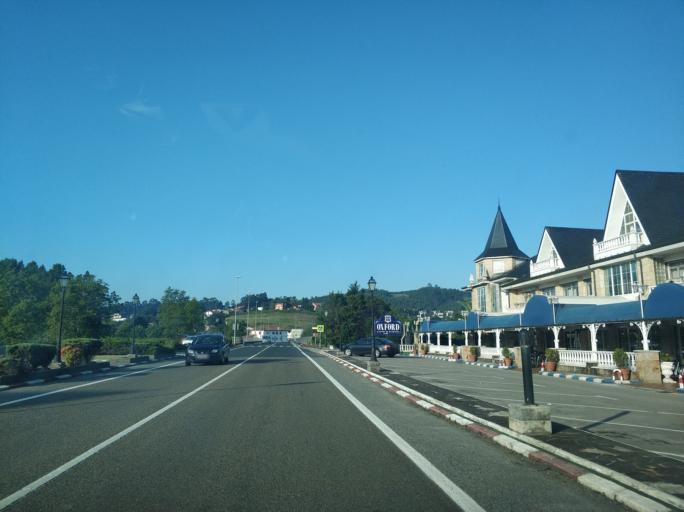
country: ES
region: Cantabria
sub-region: Provincia de Cantabria
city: Miengo
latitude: 43.4049
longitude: -3.9492
